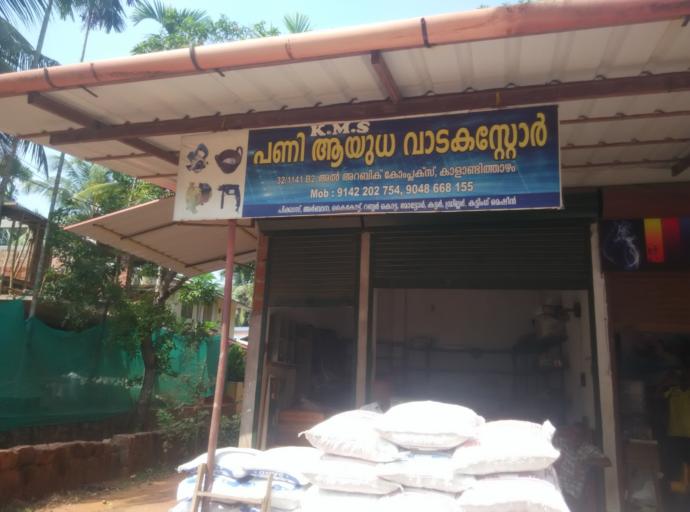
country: IN
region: Kerala
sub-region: Kozhikode
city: Kunnamangalam
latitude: 11.2849
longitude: 75.8340
